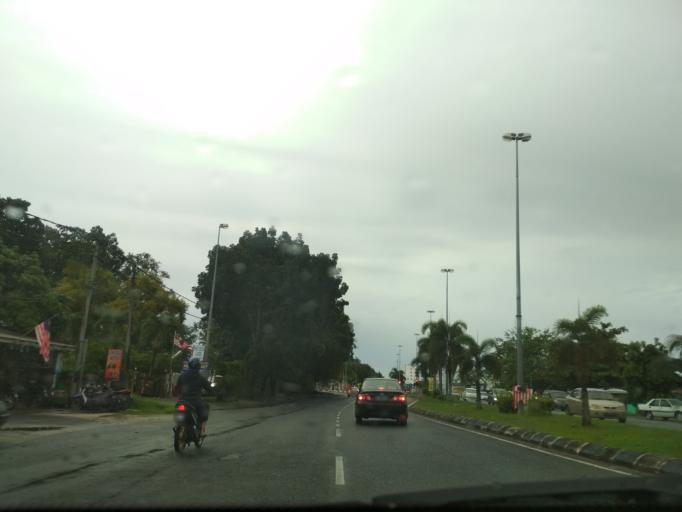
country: MY
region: Perlis
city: Kangar
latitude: 6.4260
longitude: 100.1846
